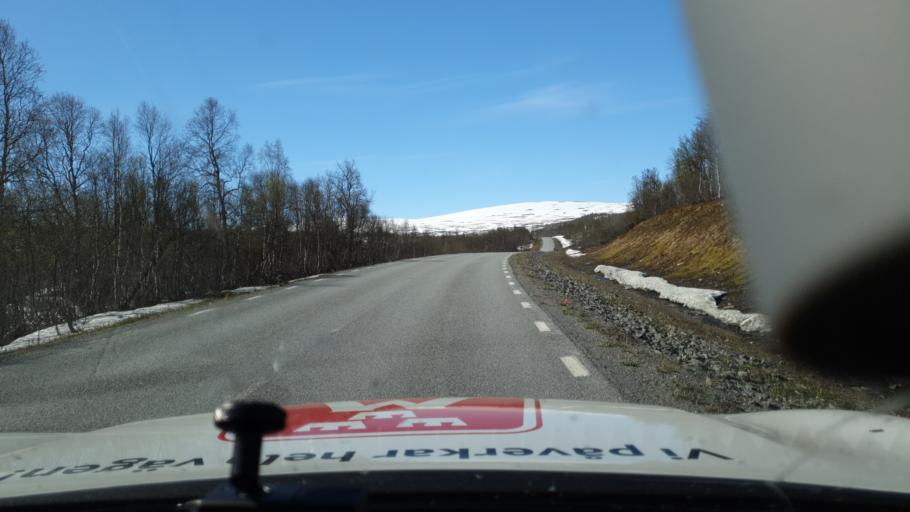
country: NO
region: Nordland
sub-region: Hattfjelldal
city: Hattfjelldal
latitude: 65.7011
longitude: 14.5987
